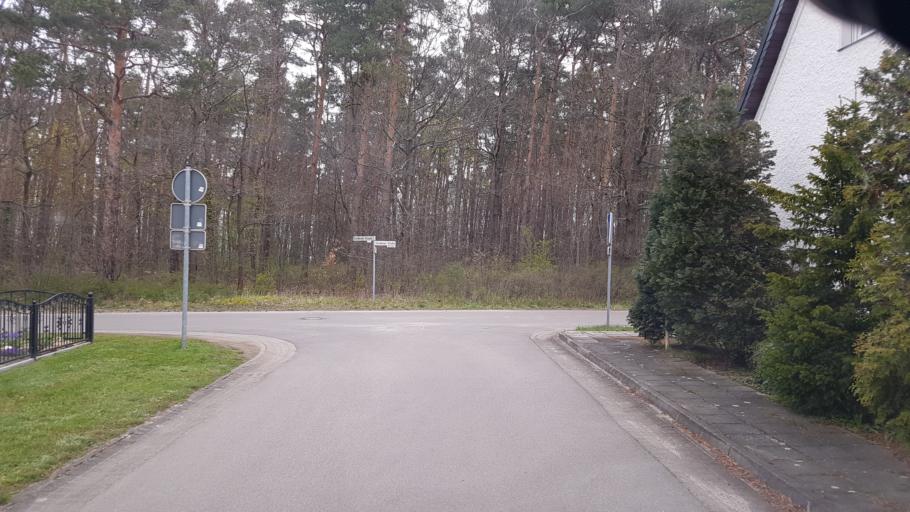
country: DE
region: Brandenburg
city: Plessa
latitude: 51.4826
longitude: 13.5986
